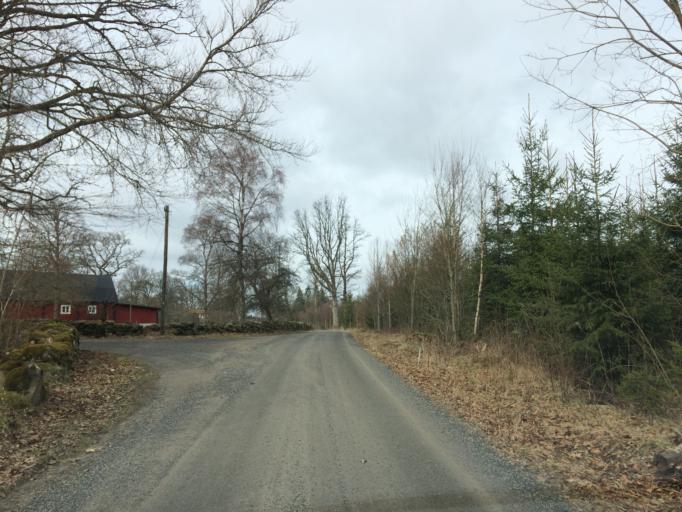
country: SE
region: Skane
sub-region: Osby Kommun
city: Lonsboda
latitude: 56.4053
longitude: 14.3321
